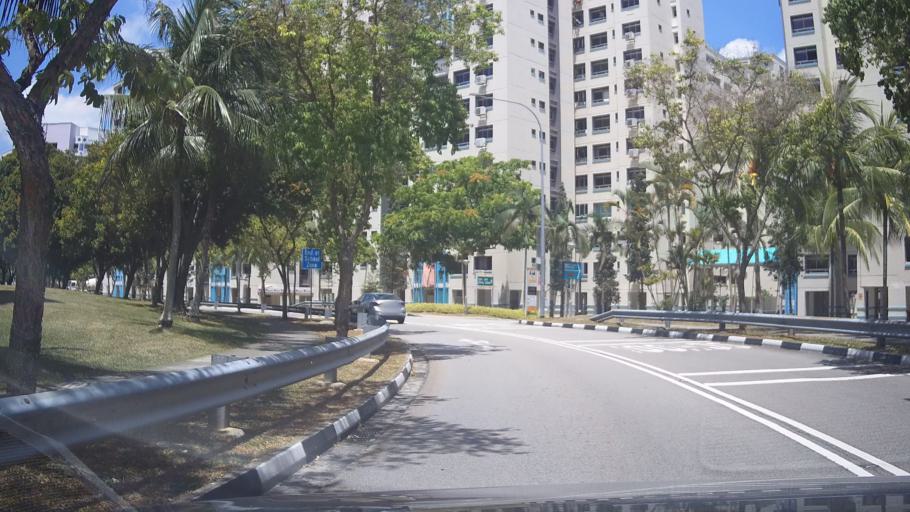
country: MY
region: Johor
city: Kampung Pasir Gudang Baru
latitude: 1.3725
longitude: 103.9623
